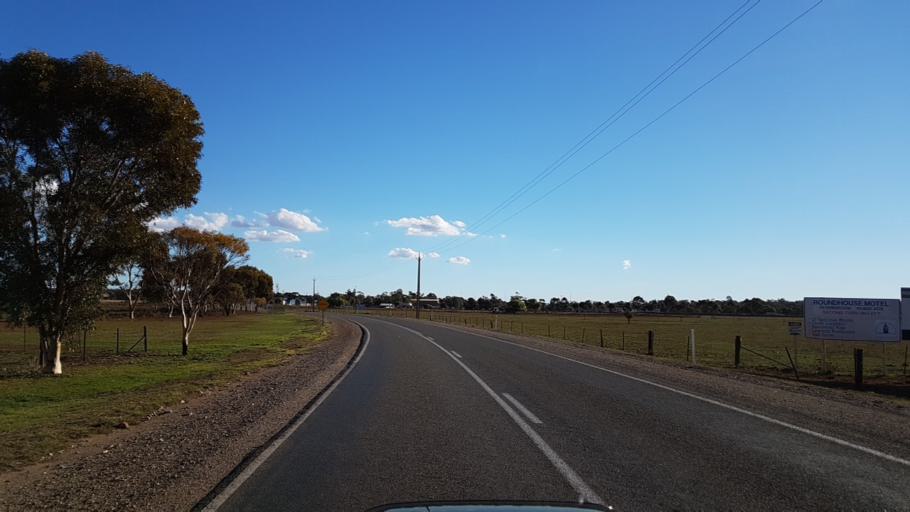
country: AU
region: South Australia
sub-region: Peterborough
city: Peterborough
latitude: -32.9705
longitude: 138.8523
